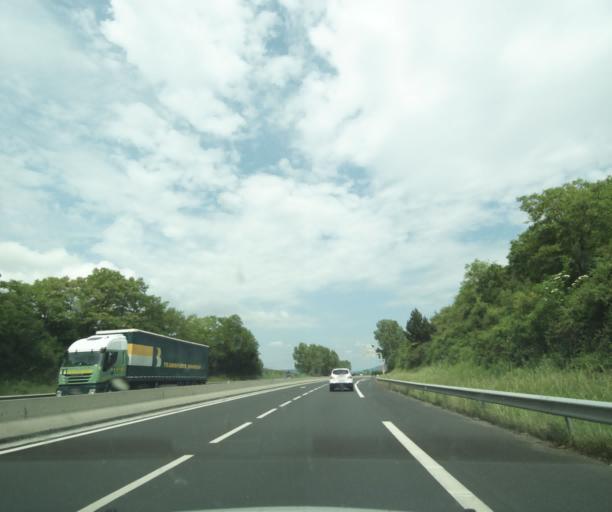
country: FR
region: Auvergne
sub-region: Departement du Puy-de-Dome
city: Le Crest
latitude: 45.6851
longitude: 3.1445
